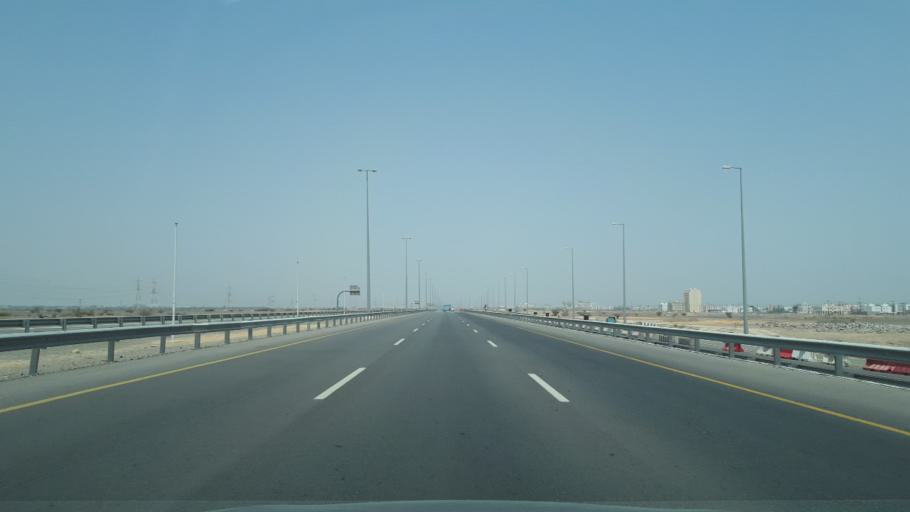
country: OM
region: Muhafazat Masqat
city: As Sib al Jadidah
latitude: 23.6295
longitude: 58.0704
